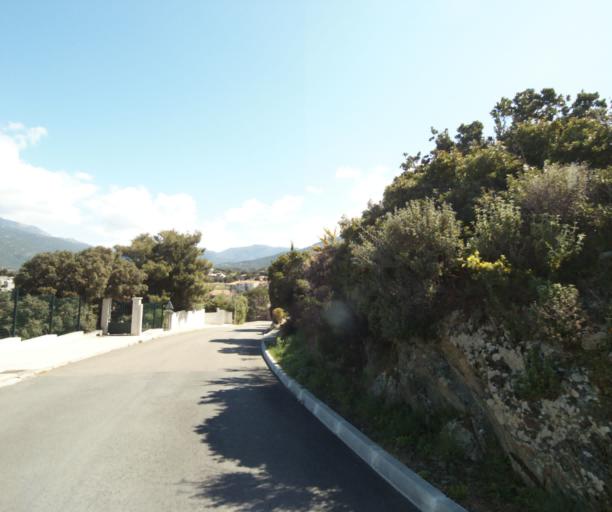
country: FR
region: Corsica
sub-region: Departement de la Corse-du-Sud
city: Propriano
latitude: 41.6765
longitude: 8.9110
